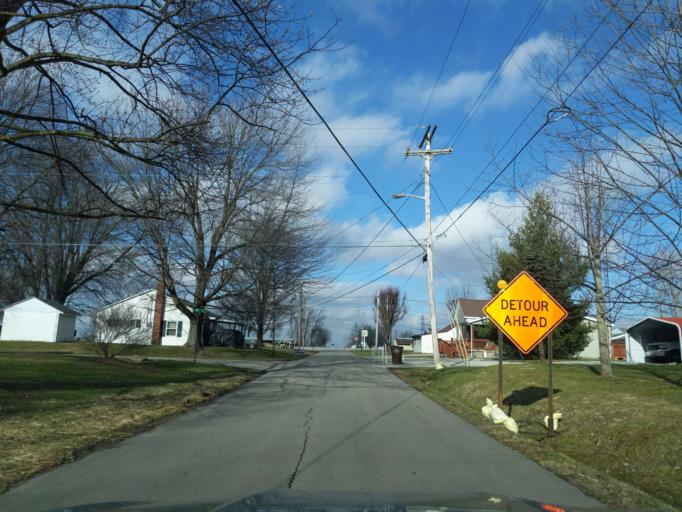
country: US
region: Indiana
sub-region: Ripley County
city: Batesville
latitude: 39.3099
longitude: -85.3259
